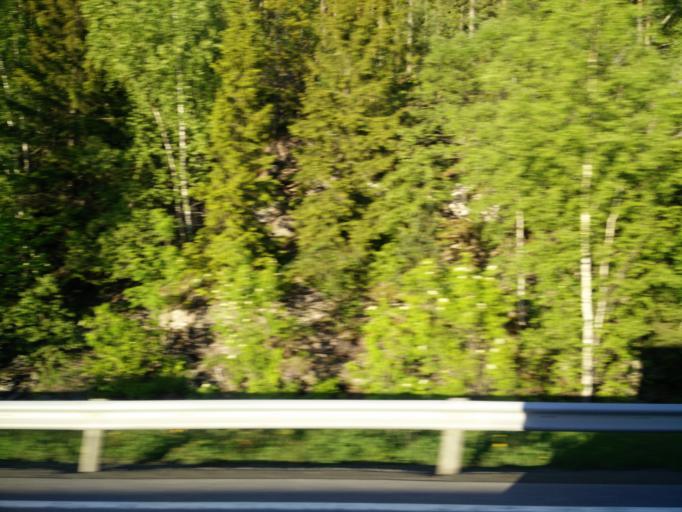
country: NO
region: Buskerud
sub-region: Hole
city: Vik
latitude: 60.0153
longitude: 10.2688
